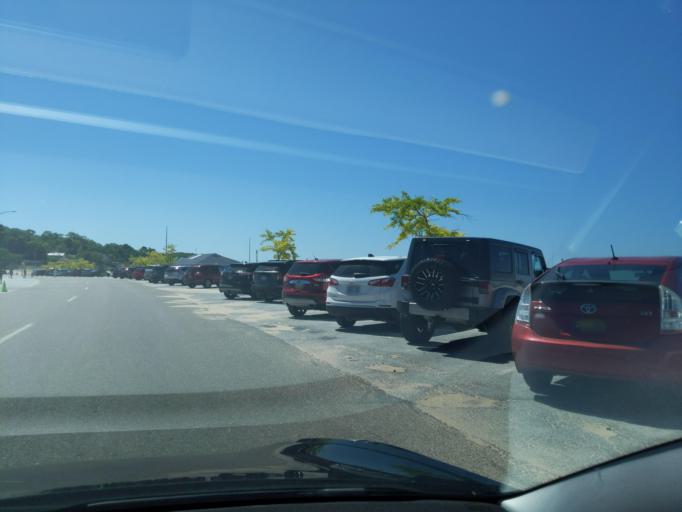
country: US
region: Michigan
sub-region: Muskegon County
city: Roosevelt Park
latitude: 43.2241
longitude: -86.3360
